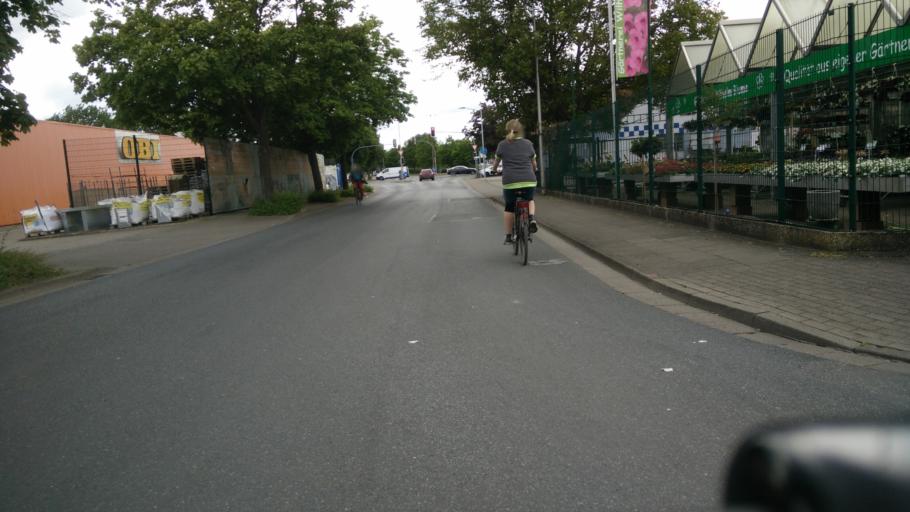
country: DE
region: Lower Saxony
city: Wunstorf
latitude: 52.4296
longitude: 9.4149
